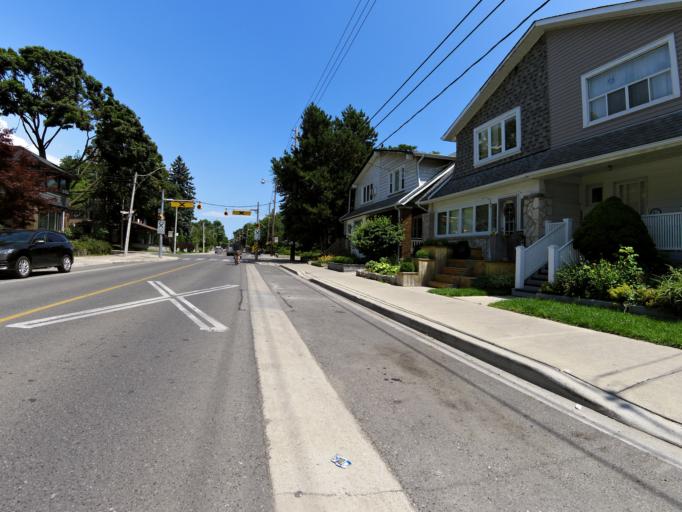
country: CA
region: Ontario
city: Toronto
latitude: 43.6733
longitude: -79.3174
